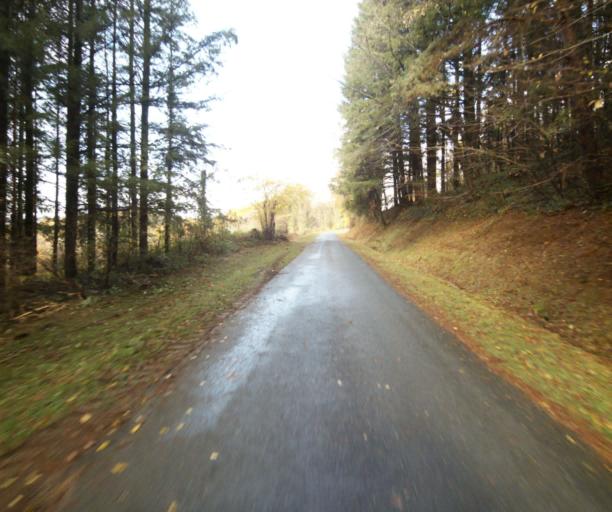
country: FR
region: Limousin
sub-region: Departement de la Correze
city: Cornil
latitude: 45.2162
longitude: 1.6574
